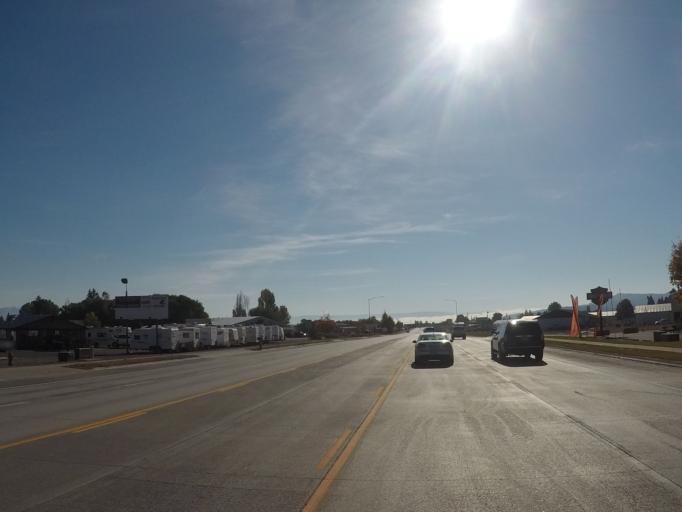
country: US
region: Montana
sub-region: Flathead County
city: Kalispell
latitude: 48.1733
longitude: -114.2964
